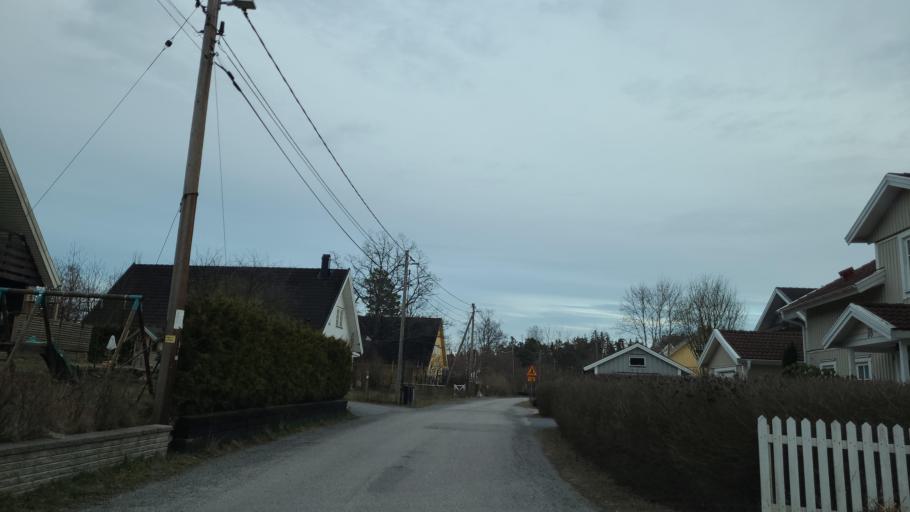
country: SE
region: Stockholm
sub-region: Nacka Kommun
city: Boo
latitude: 59.3198
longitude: 18.2642
